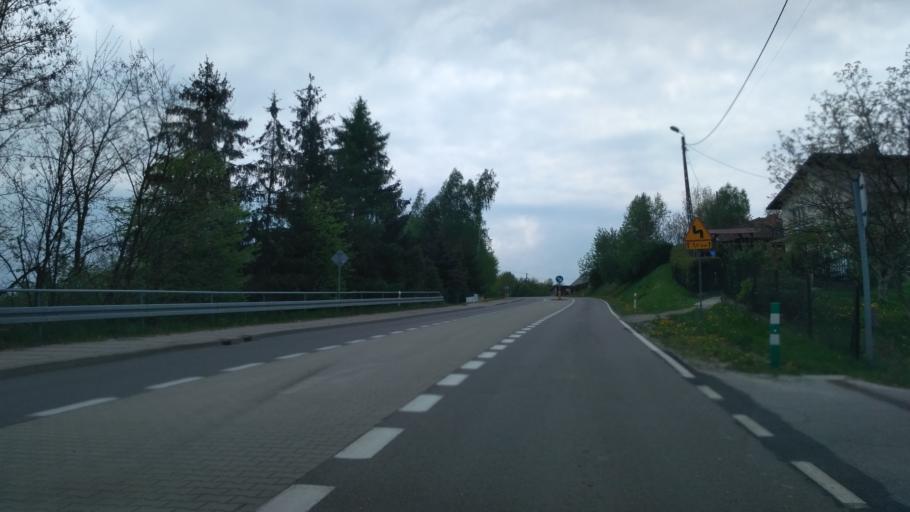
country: PL
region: Lesser Poland Voivodeship
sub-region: Powiat tarnowski
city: Tarnowiec
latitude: 49.9542
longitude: 21.0065
